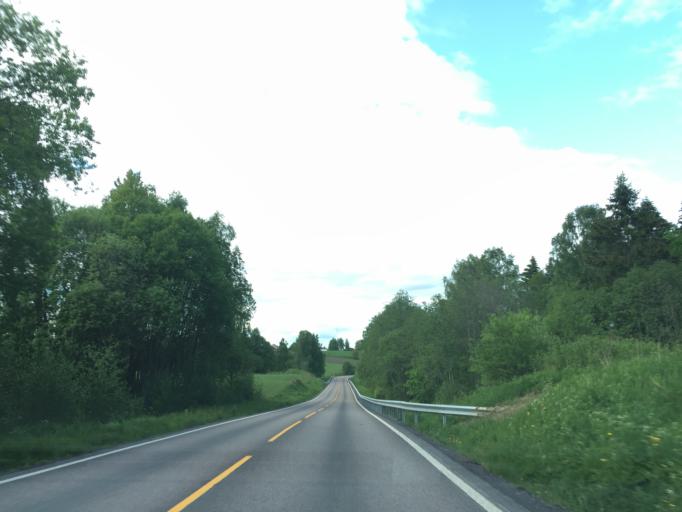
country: NO
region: Akershus
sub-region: Fet
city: Fetsund
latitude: 59.9395
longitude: 11.1902
